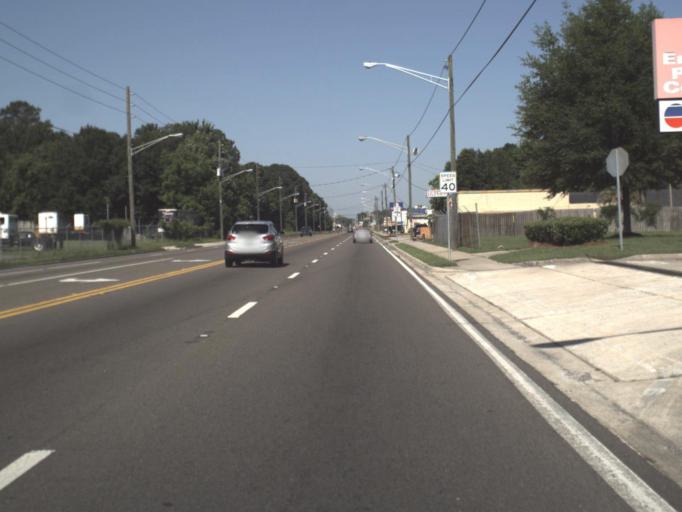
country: US
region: Florida
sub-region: Duval County
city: Jacksonville
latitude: 30.3289
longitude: -81.7228
